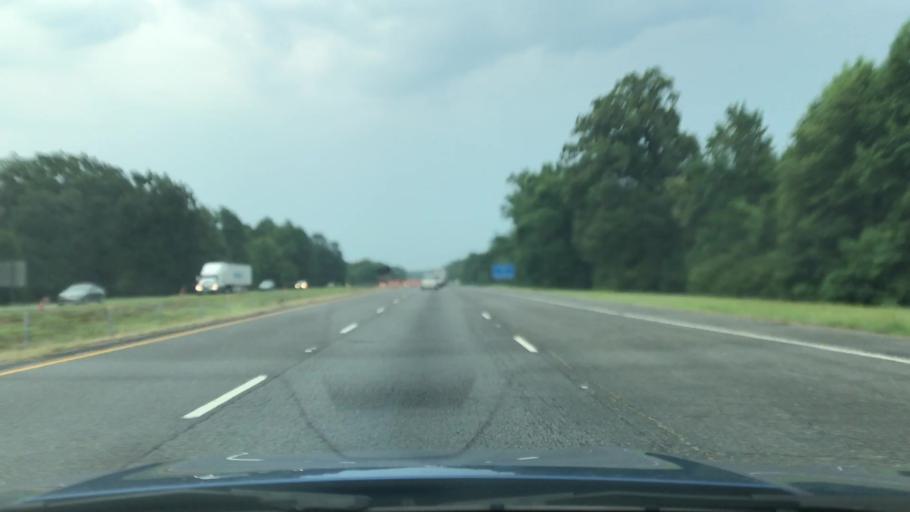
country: US
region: Texas
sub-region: Harrison County
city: Waskom
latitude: 32.4609
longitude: -94.0426
